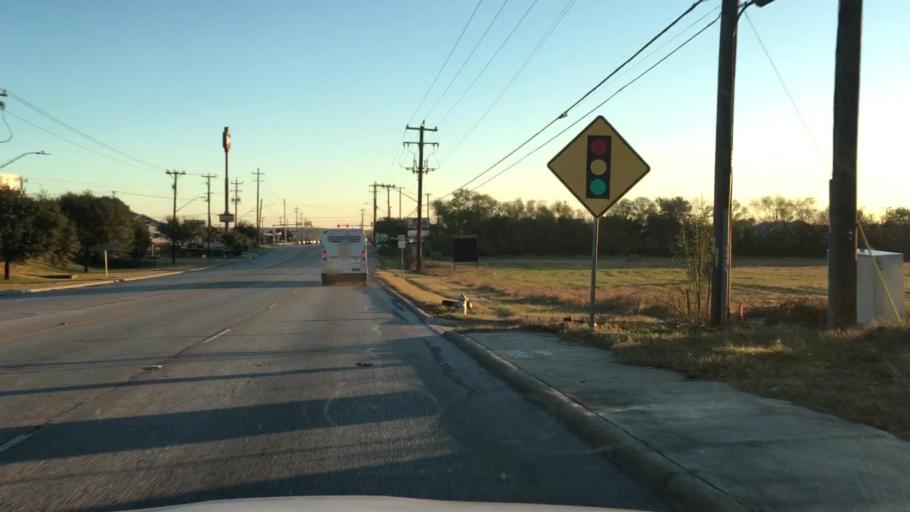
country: US
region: Texas
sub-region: Bexar County
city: Live Oak
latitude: 29.5902
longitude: -98.3549
